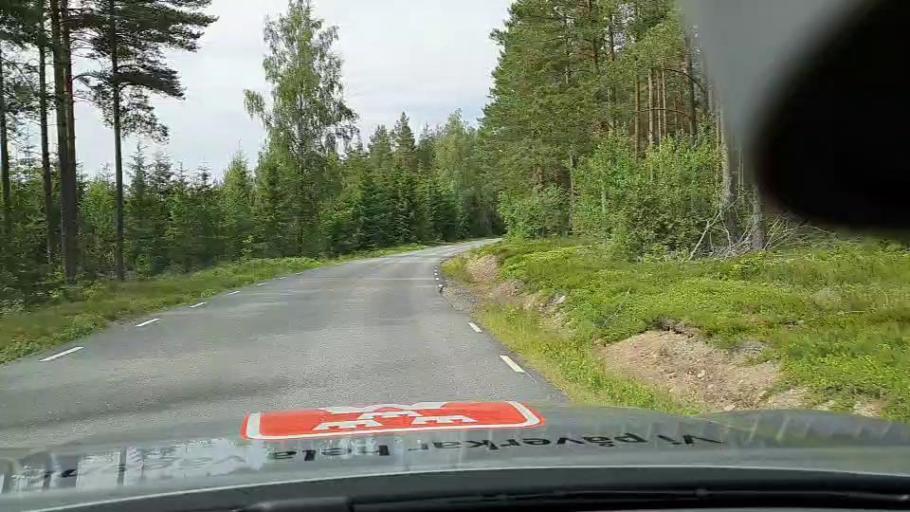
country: SE
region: Soedermanland
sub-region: Eskilstuna Kommun
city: Arla
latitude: 59.2322
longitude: 16.7266
